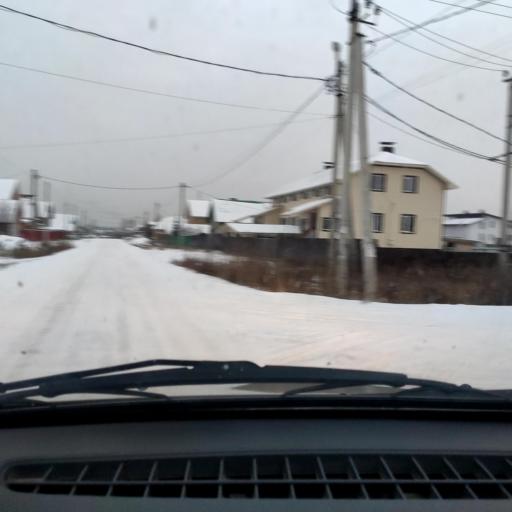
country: RU
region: Bashkortostan
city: Mikhaylovka
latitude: 54.7911
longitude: 55.8278
